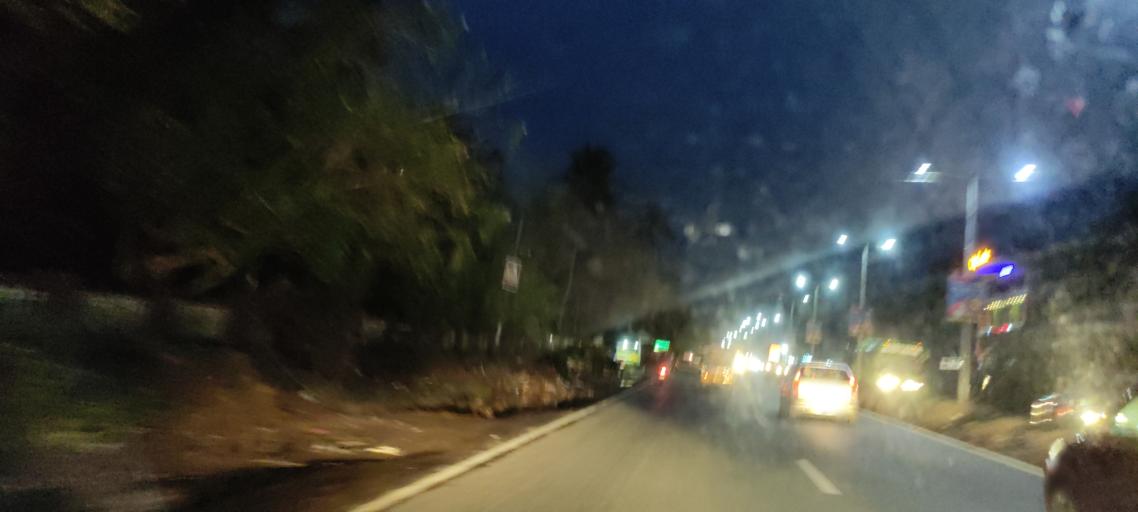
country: IN
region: Kerala
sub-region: Alappuzha
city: Arukutti
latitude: 9.8631
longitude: 76.3058
